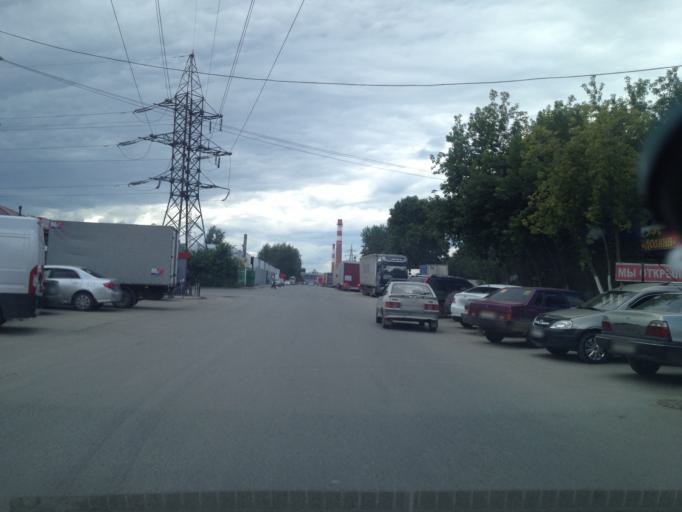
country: RU
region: Sverdlovsk
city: Yekaterinburg
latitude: 56.8623
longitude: 60.5357
